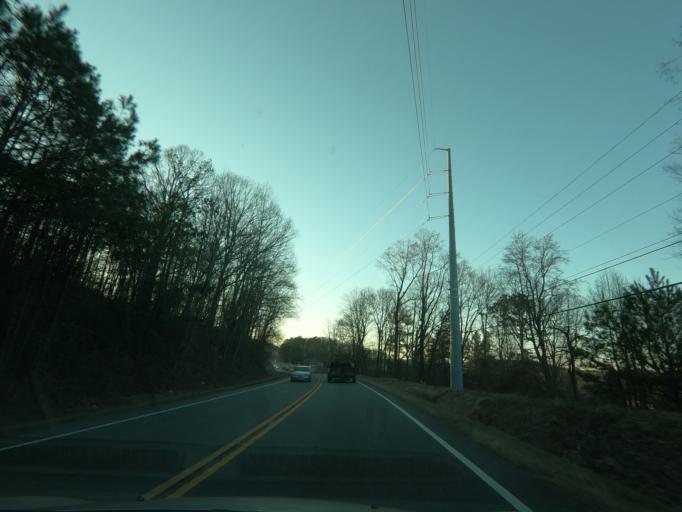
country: US
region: Georgia
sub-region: Forsyth County
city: Cumming
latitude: 34.3047
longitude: -84.2030
